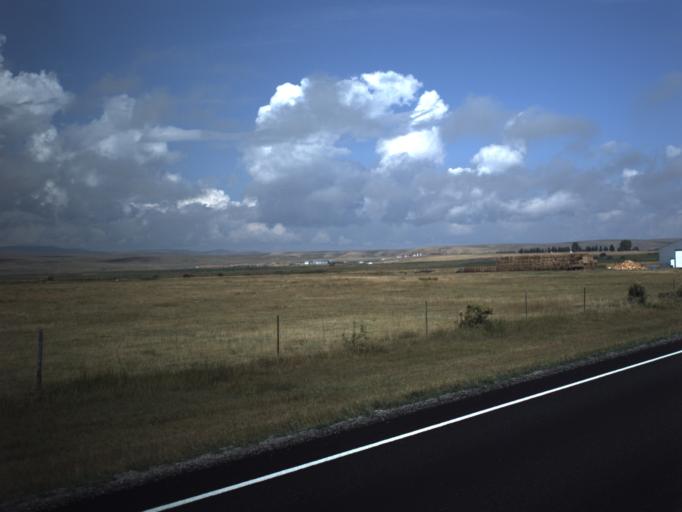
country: US
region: Utah
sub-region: Rich County
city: Randolph
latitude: 41.6516
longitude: -111.1845
